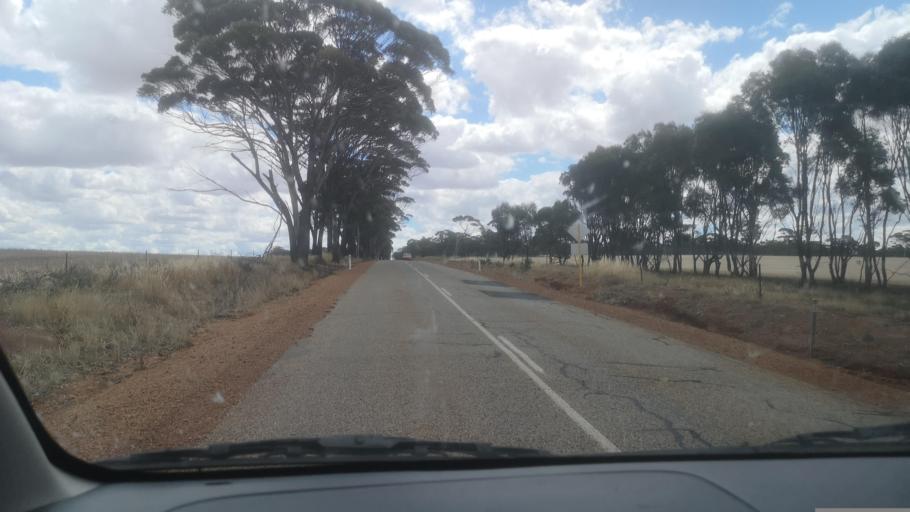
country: AU
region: Western Australia
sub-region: Beverley
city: Beverley
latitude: -31.9899
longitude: 117.1181
